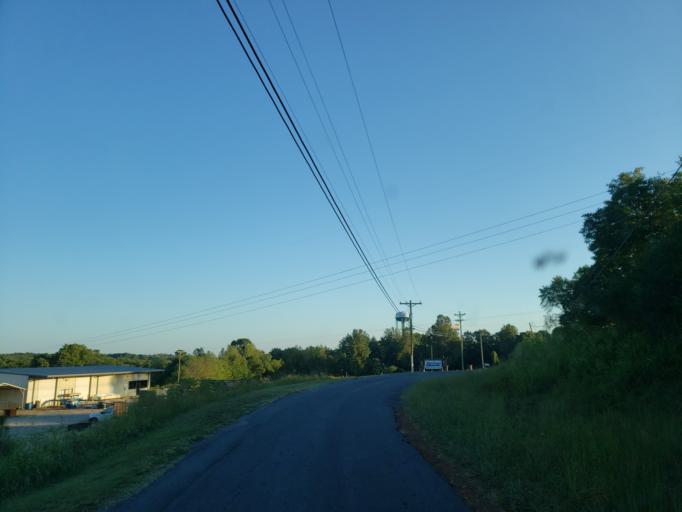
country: US
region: Georgia
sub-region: Pickens County
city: Jasper
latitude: 34.4306
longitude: -84.4308
